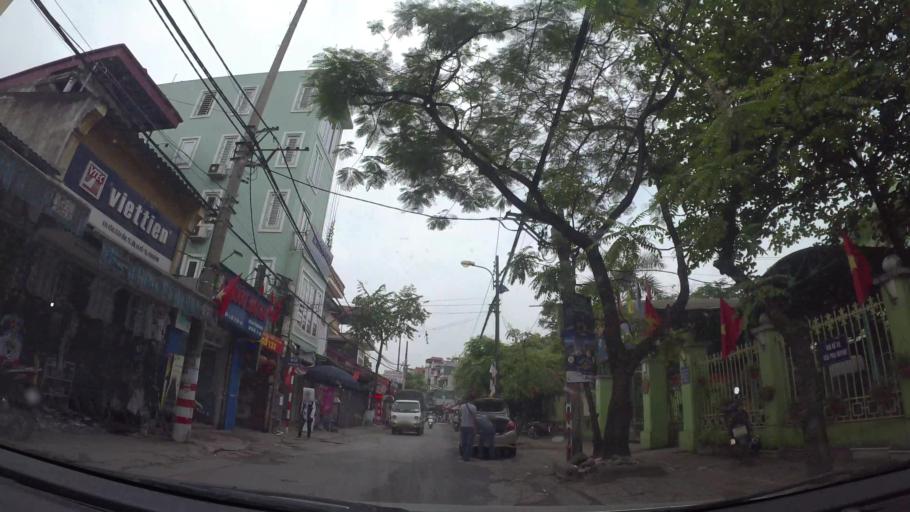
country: VN
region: Ha Noi
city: Tay Ho
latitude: 21.0710
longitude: 105.7994
